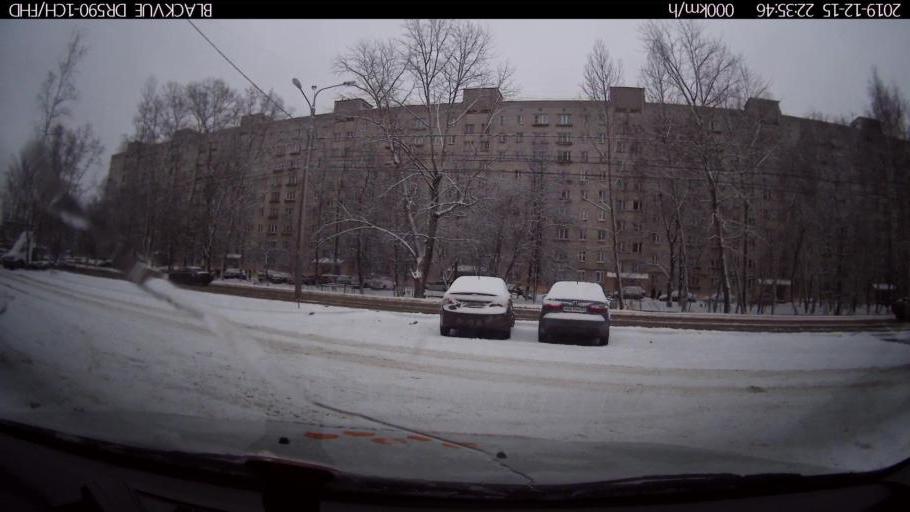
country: RU
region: Nizjnij Novgorod
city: Gorbatovka
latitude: 56.3422
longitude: 43.8297
